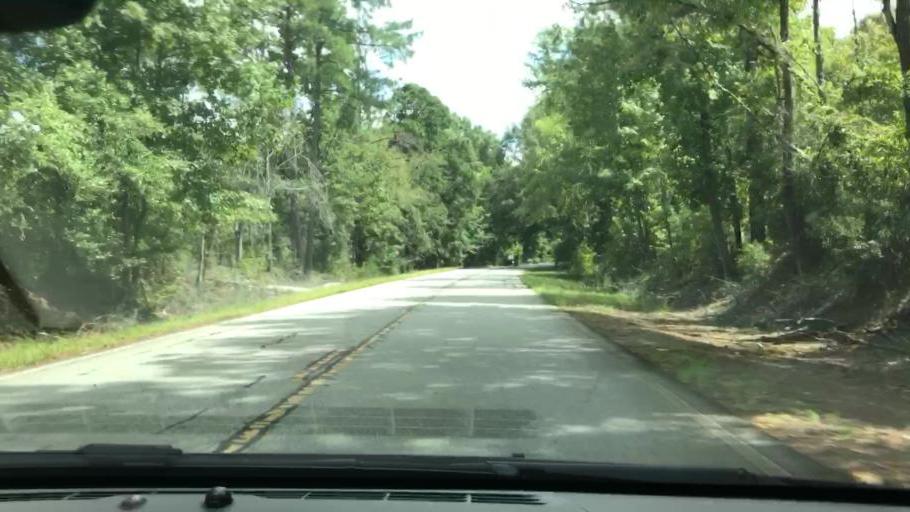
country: US
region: Georgia
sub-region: Quitman County
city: Georgetown
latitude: 32.0400
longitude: -85.0300
